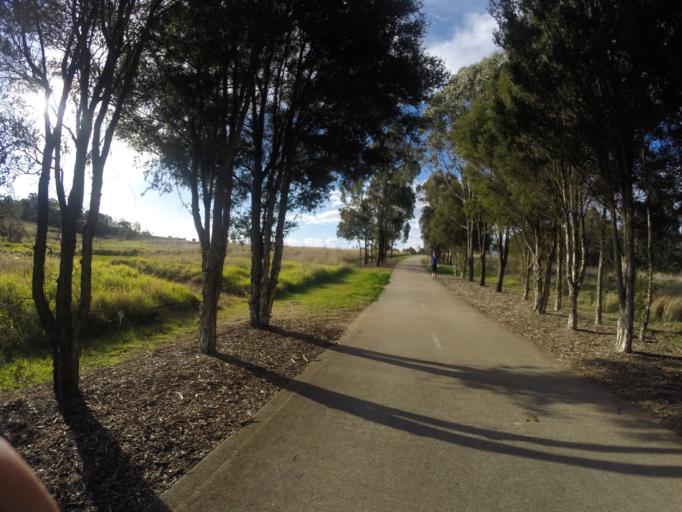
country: AU
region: New South Wales
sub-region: Fairfield
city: Horsley Park
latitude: -33.8570
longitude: 150.8689
